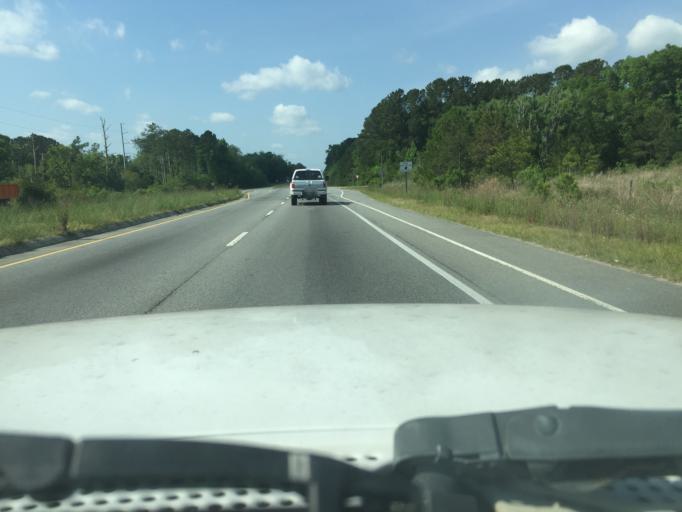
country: US
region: Georgia
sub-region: Chatham County
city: Georgetown
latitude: 32.0178
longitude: -81.2304
